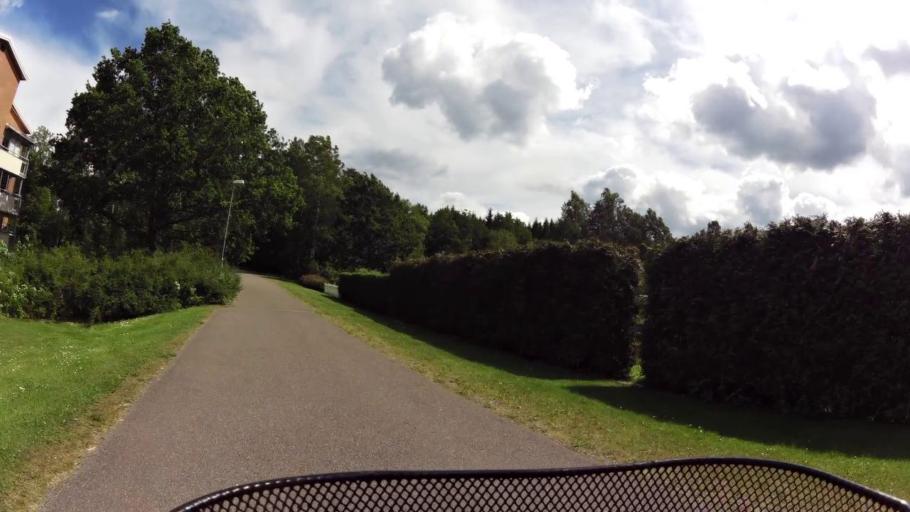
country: SE
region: OEstergoetland
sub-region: Linkopings Kommun
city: Malmslatt
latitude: 58.4196
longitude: 15.5056
